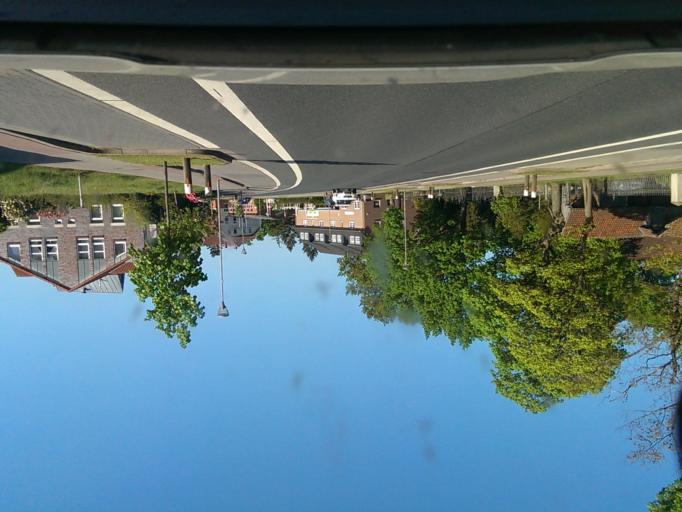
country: DE
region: Lower Saxony
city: Wietze
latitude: 52.6529
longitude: 9.8436
